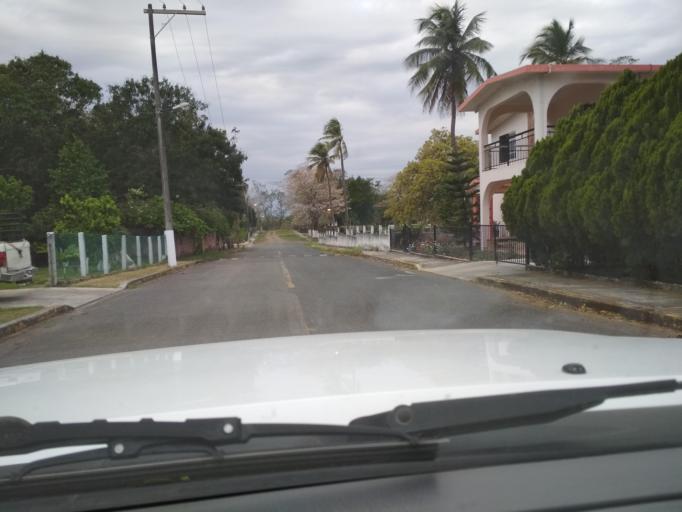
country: MX
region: Veracruz
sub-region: Veracruz
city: Delfino Victoria (Santa Fe)
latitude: 19.1592
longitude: -96.2941
